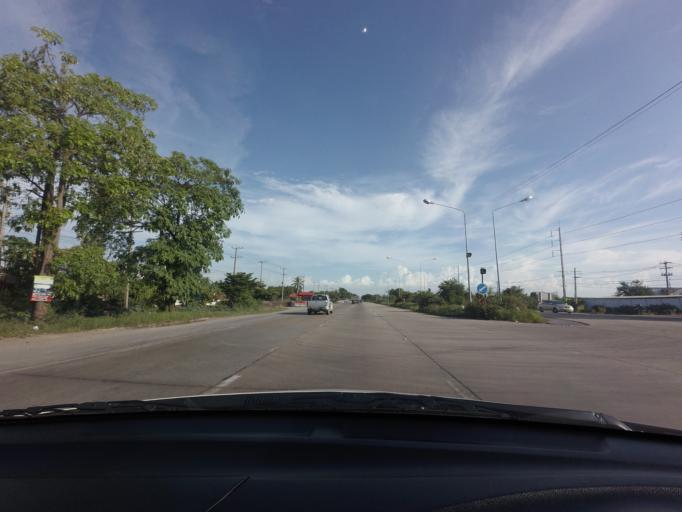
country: TH
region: Phra Nakhon Si Ayutthaya
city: Lat Bua Luang
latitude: 14.1554
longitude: 100.2909
